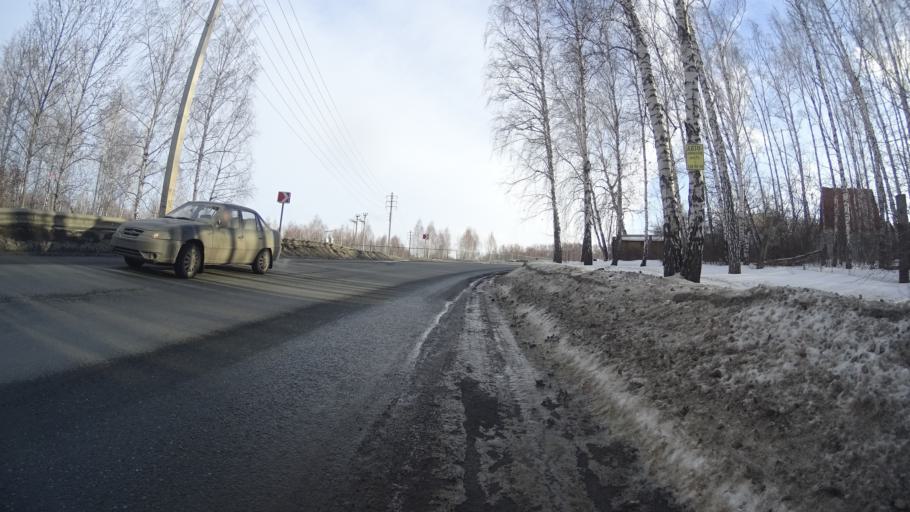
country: RU
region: Chelyabinsk
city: Sargazy
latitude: 55.1286
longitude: 61.2886
